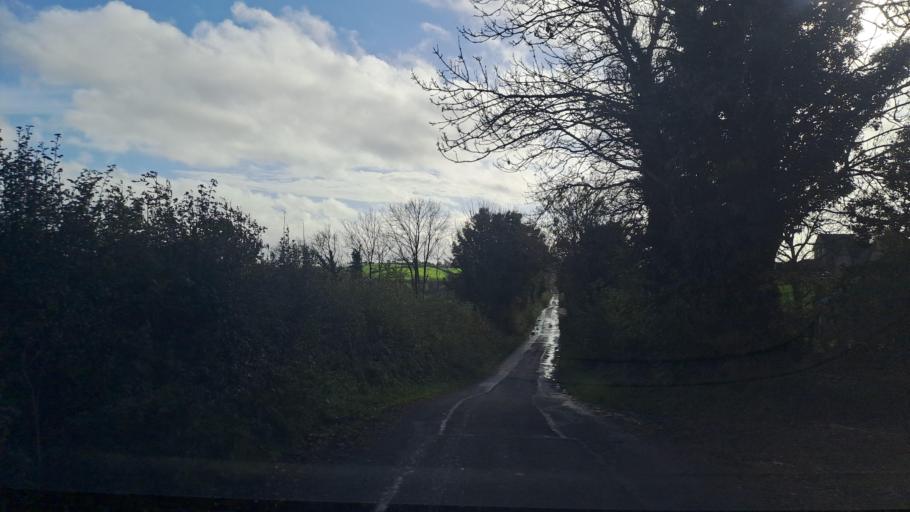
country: IE
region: Ulster
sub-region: An Cabhan
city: Cootehill
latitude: 53.9987
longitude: -7.0280
